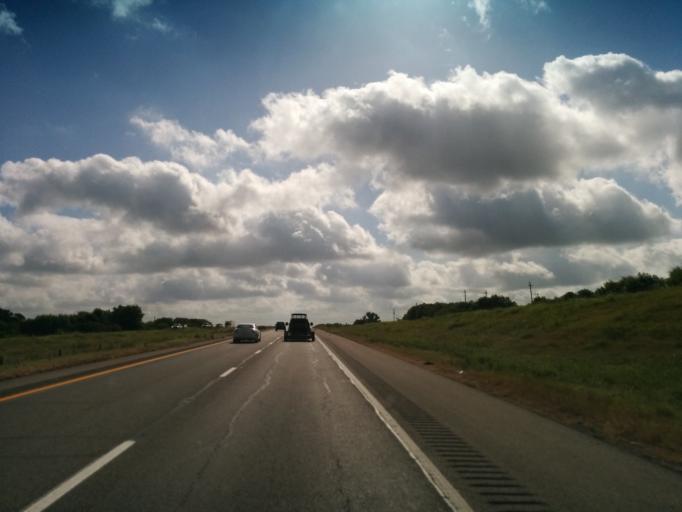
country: US
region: Texas
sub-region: Caldwell County
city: Luling
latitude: 29.6338
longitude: -97.7382
